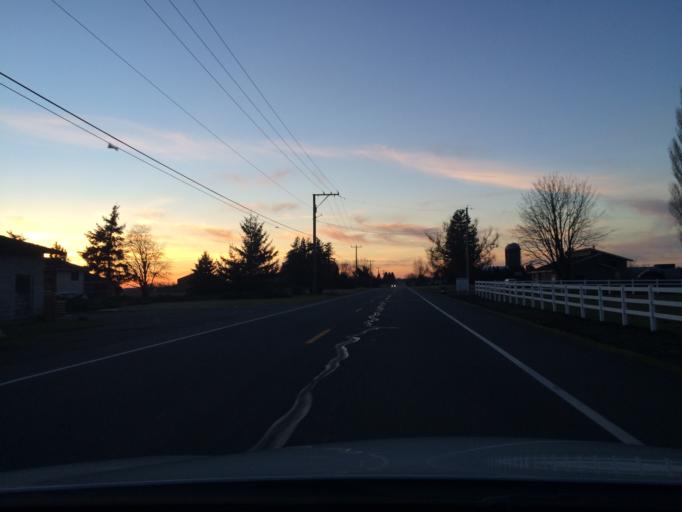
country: US
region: Washington
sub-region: Whatcom County
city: Everson
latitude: 48.9419
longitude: -122.3794
